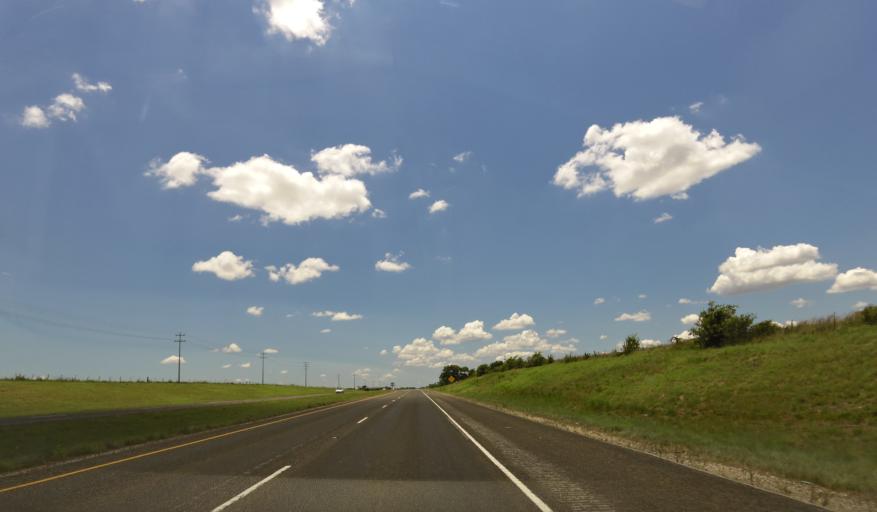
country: US
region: Texas
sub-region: Burleson County
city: Somerville
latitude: 30.1681
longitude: -96.6106
